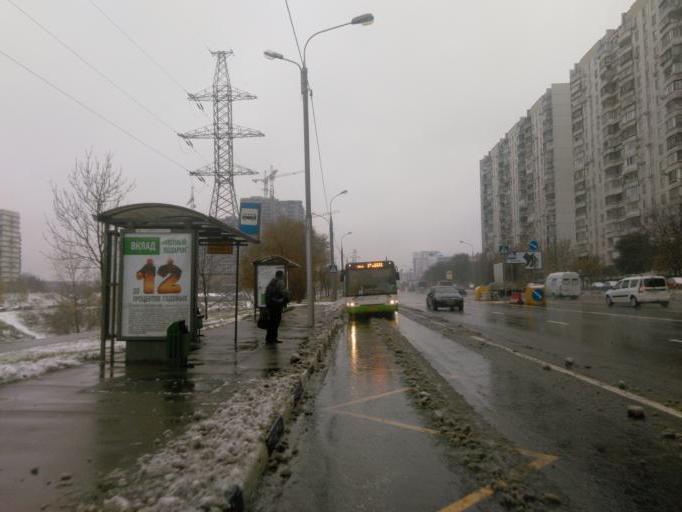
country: RU
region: Moscow
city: Kotlovka
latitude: 55.6416
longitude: 37.5990
